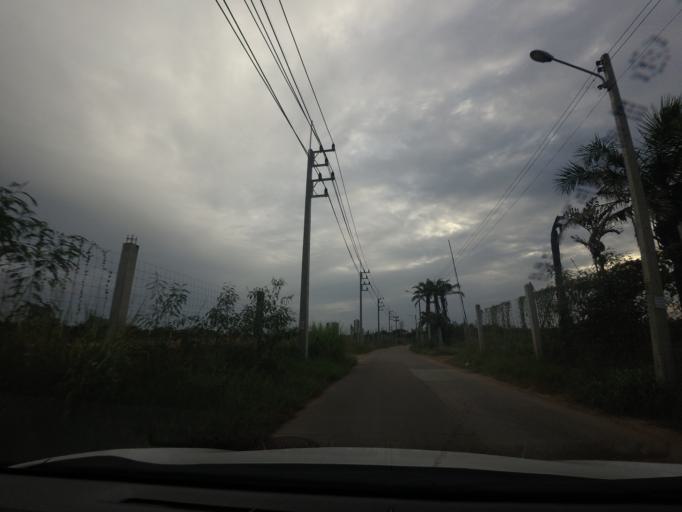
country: TH
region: Chon Buri
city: Phatthaya
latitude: 12.9017
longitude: 100.8916
